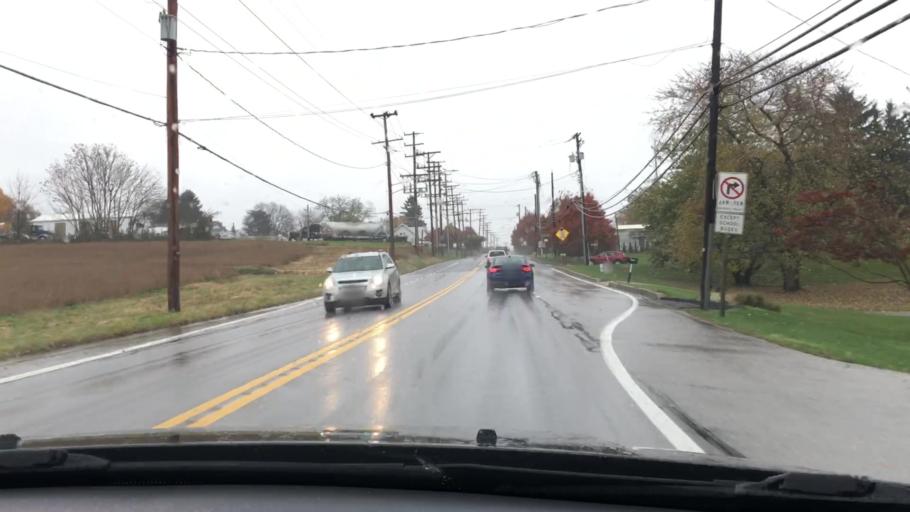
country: US
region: Maryland
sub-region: Carroll County
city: Manchester
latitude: 39.6678
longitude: -76.8894
